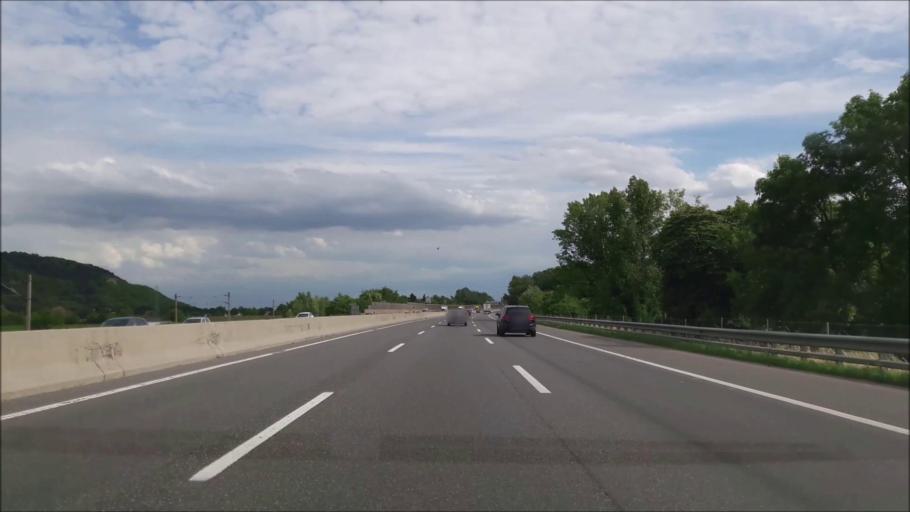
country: AT
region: Lower Austria
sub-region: Politischer Bezirk Korneuburg
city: Bisamberg
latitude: 48.3237
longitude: 16.3416
